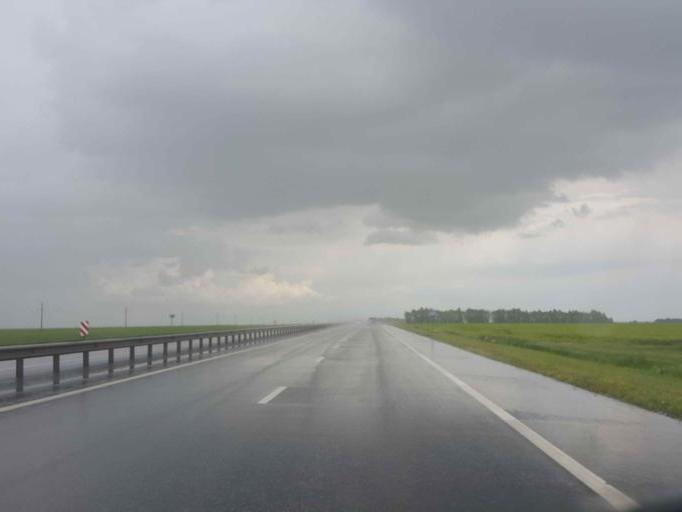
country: RU
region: Tambov
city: Zavoronezhskoye
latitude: 52.8314
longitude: 40.8847
